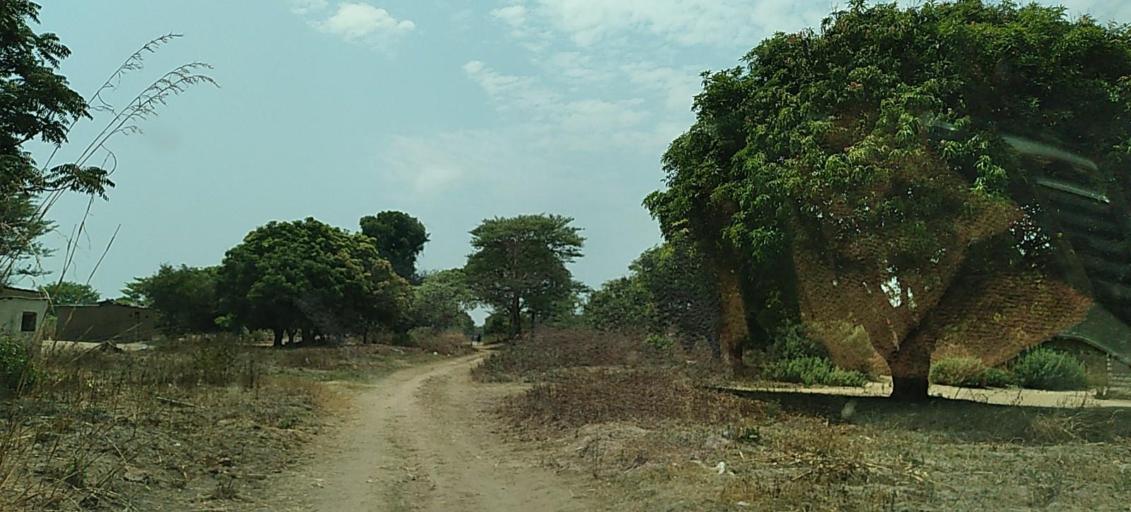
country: ZM
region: Copperbelt
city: Kalulushi
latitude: -12.9486
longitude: 28.1321
